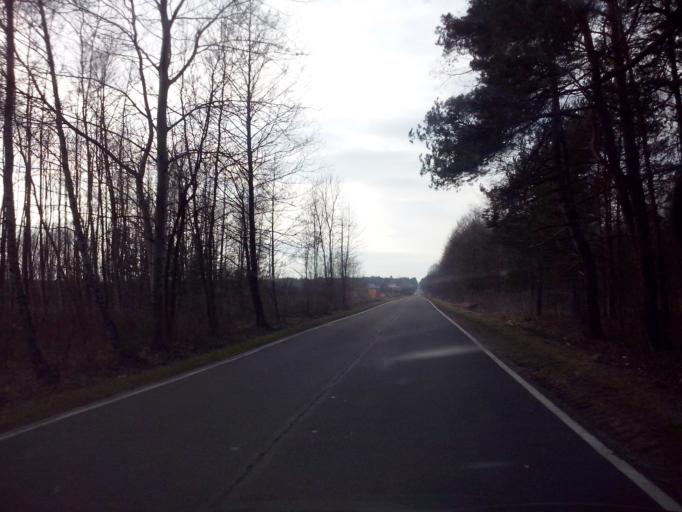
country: PL
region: Subcarpathian Voivodeship
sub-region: Powiat nizanski
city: Harasiuki
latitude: 50.4964
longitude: 22.5225
